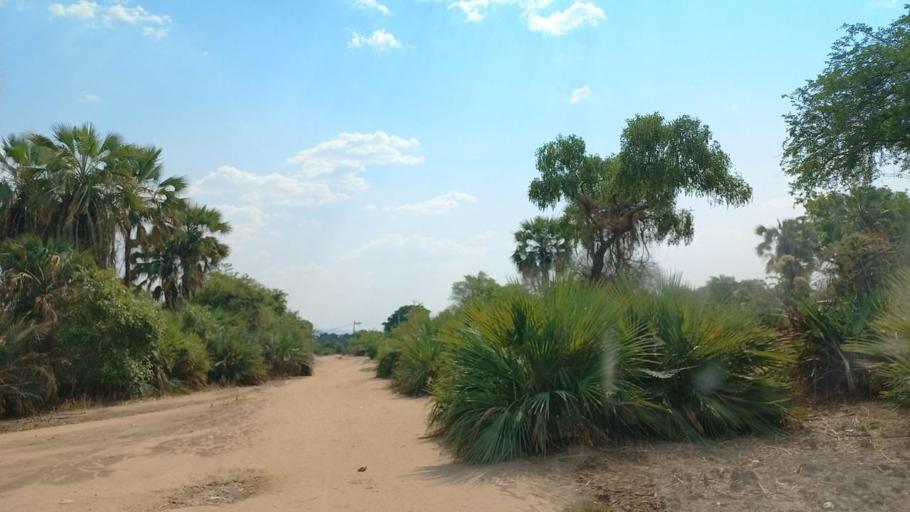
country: ZM
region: Lusaka
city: Luangwa
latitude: -15.0855
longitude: 30.1915
